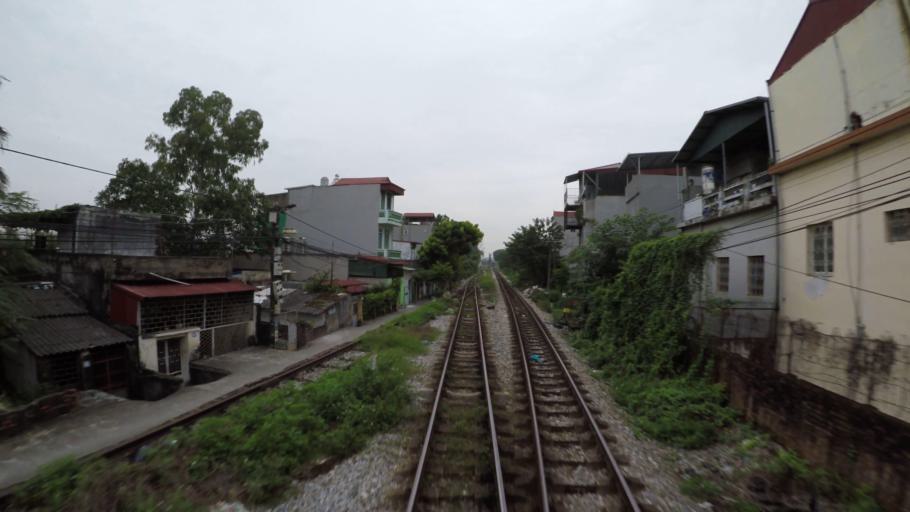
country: VN
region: Ha Noi
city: Trau Quy
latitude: 21.0372
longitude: 105.8990
